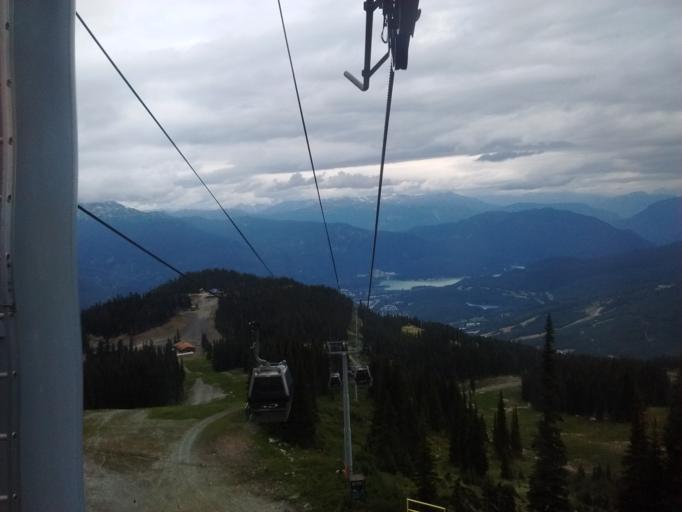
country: CA
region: British Columbia
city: Whistler
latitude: 50.0721
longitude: -122.9474
